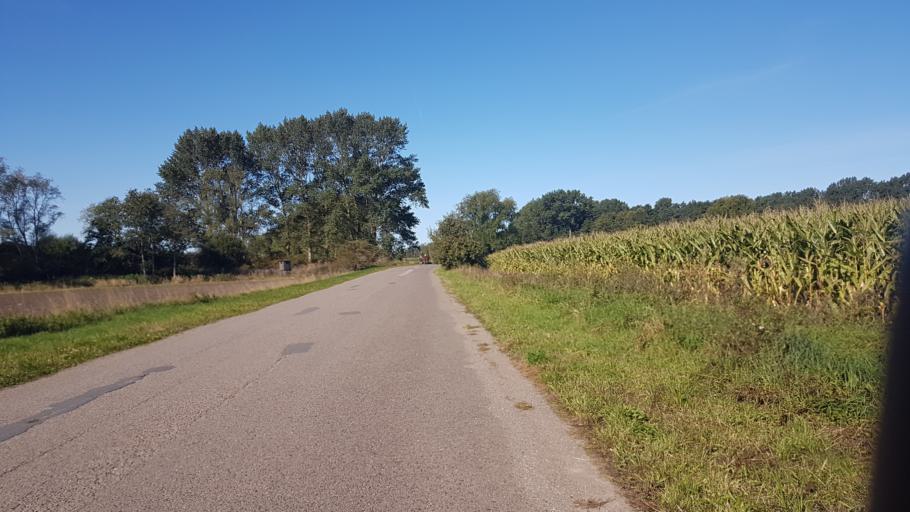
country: DE
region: Mecklenburg-Vorpommern
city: Sagard
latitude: 54.5211
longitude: 13.5209
